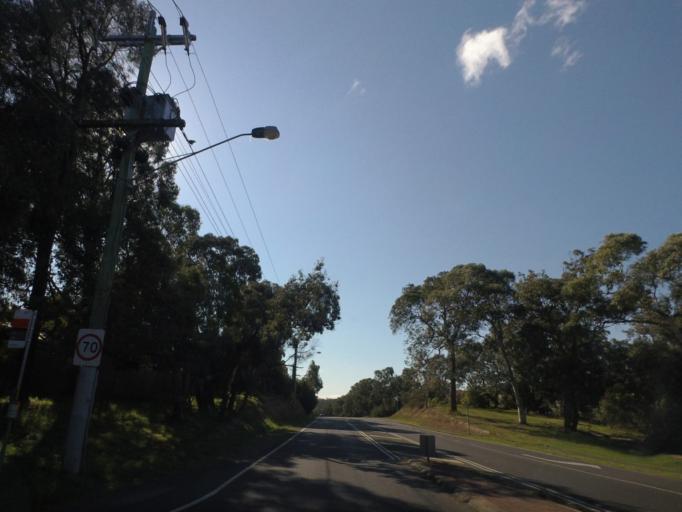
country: AU
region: Victoria
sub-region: Manningham
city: Donvale
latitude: -37.7718
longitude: 145.1836
